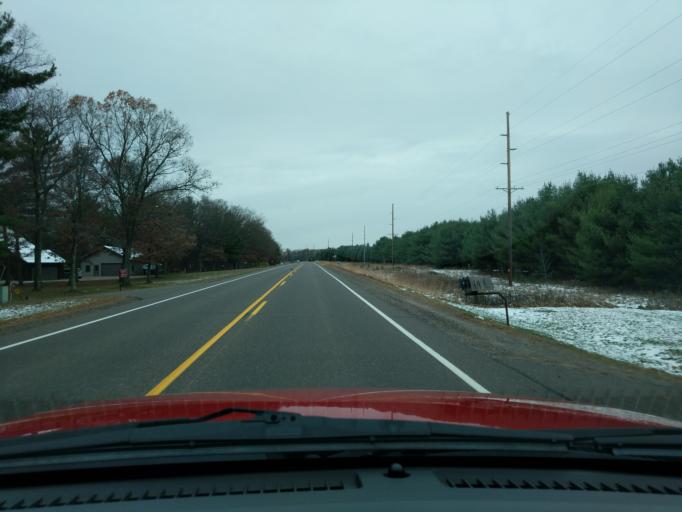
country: US
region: Wisconsin
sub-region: Burnett County
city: Siren
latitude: 45.8175
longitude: -92.2402
